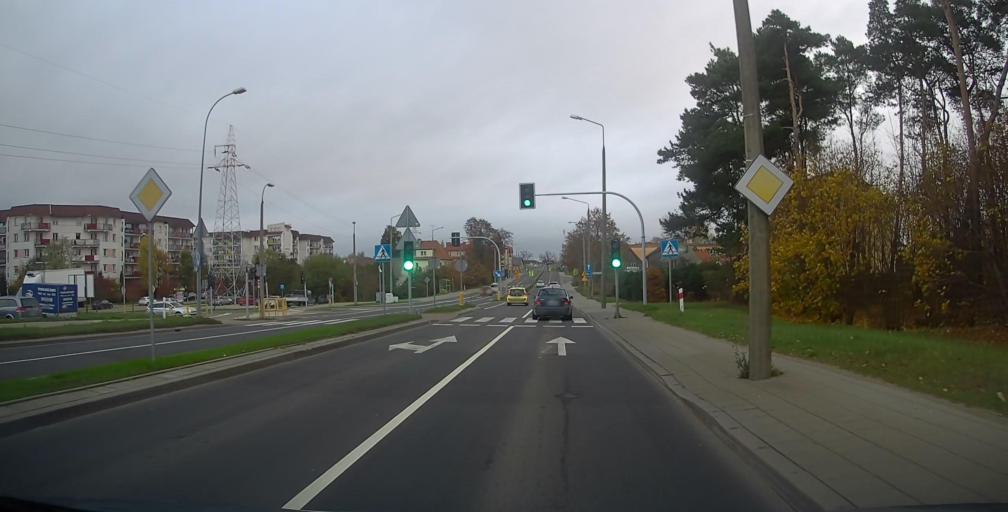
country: PL
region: Warmian-Masurian Voivodeship
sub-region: Powiat elcki
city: Elk
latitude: 53.8020
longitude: 22.3642
